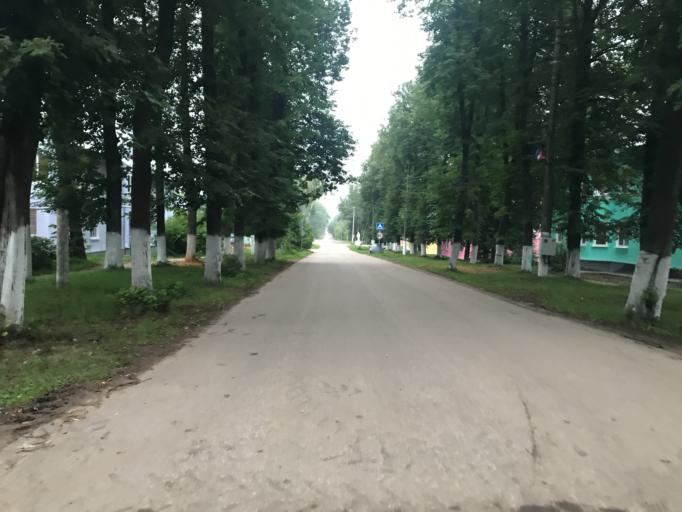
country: RU
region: Tula
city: Priupskiy
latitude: 53.9452
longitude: 37.7014
